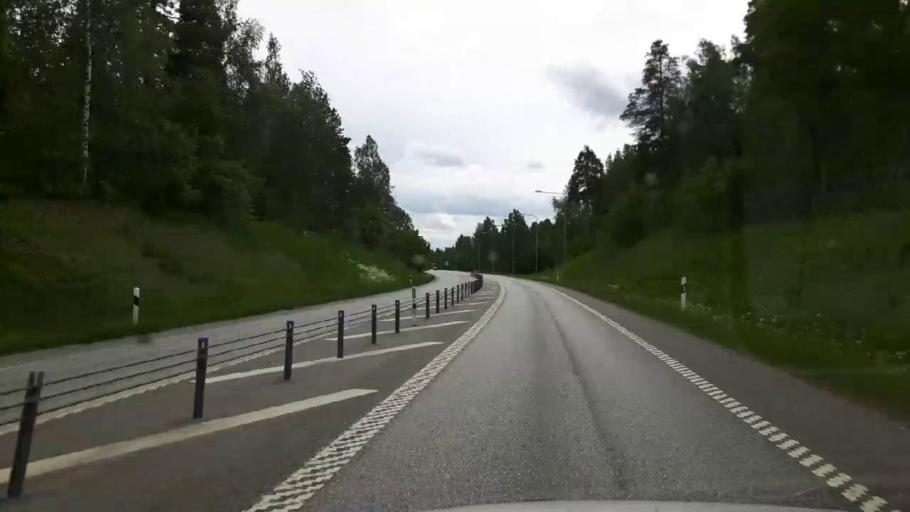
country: SE
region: Vaestmanland
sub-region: Fagersta Kommun
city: Fagersta
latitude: 60.0114
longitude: 15.7820
